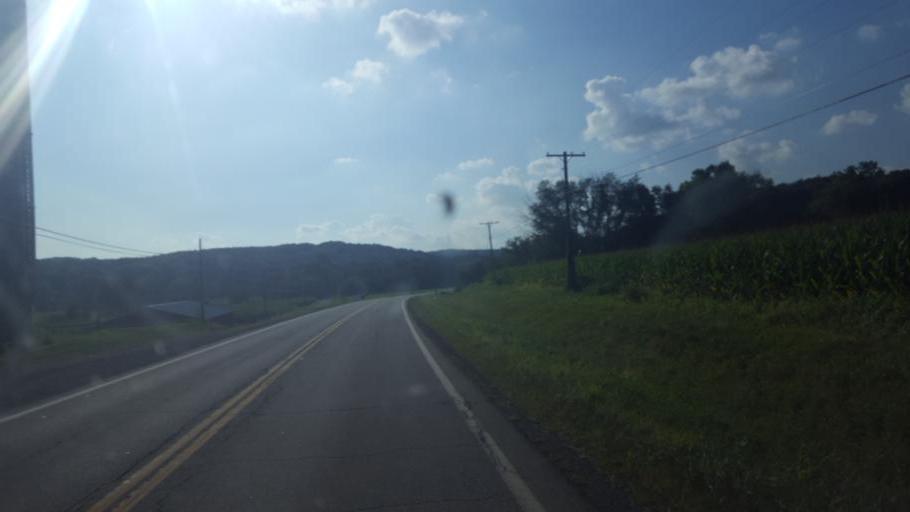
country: US
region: Ohio
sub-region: Sandusky County
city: Bellville
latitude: 40.6095
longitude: -82.4832
